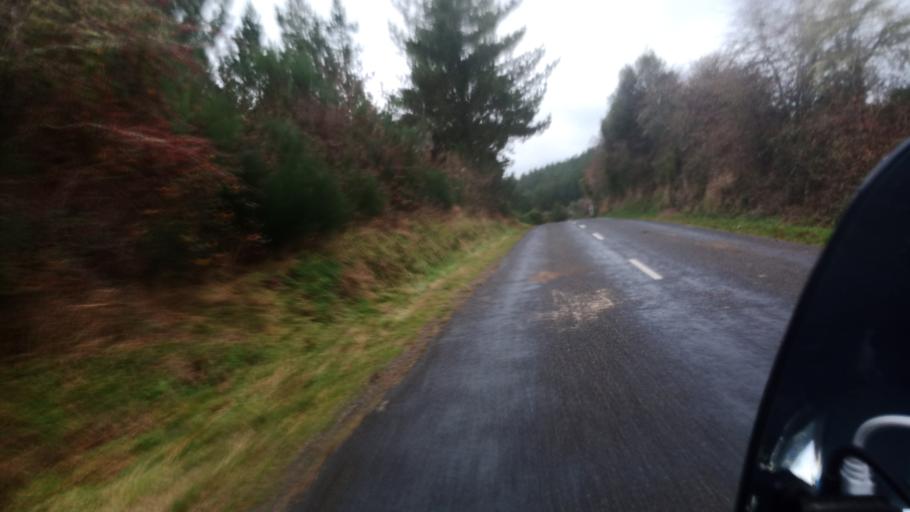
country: NZ
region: Bay of Plenty
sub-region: Whakatane District
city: Murupara
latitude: -38.6252
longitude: 176.7379
